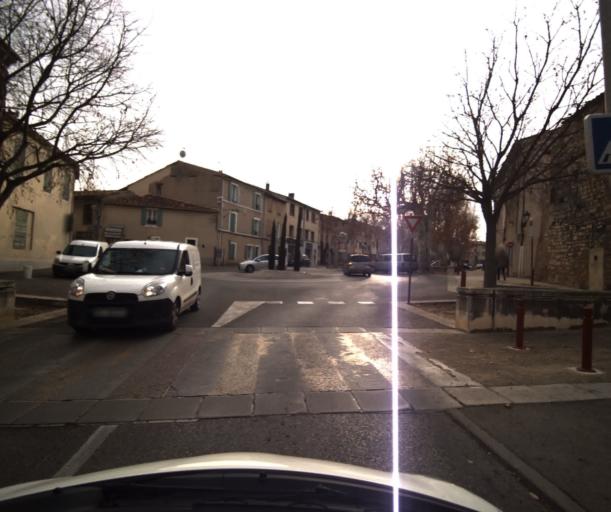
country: FR
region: Provence-Alpes-Cote d'Azur
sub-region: Departement du Vaucluse
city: Pertuis
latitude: 43.6956
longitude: 5.5052
